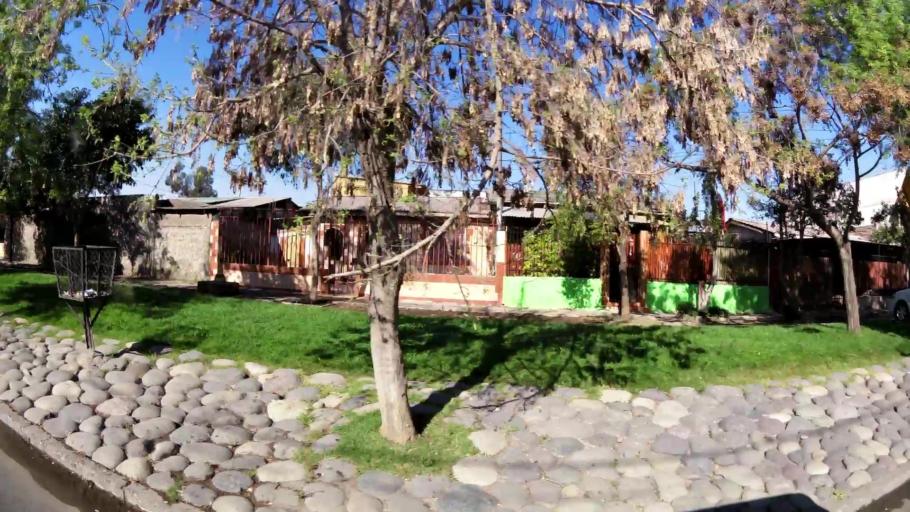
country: CL
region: Santiago Metropolitan
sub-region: Provincia de Santiago
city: La Pintana
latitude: -33.5831
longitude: -70.6501
